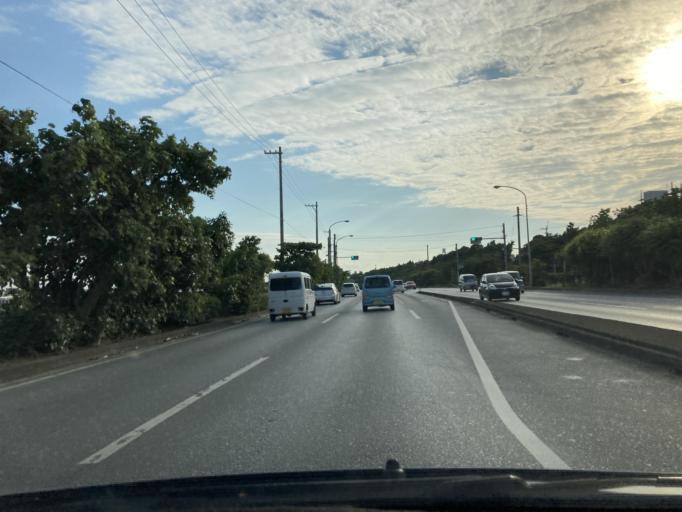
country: JP
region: Okinawa
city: Okinawa
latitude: 26.3293
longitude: 127.8362
